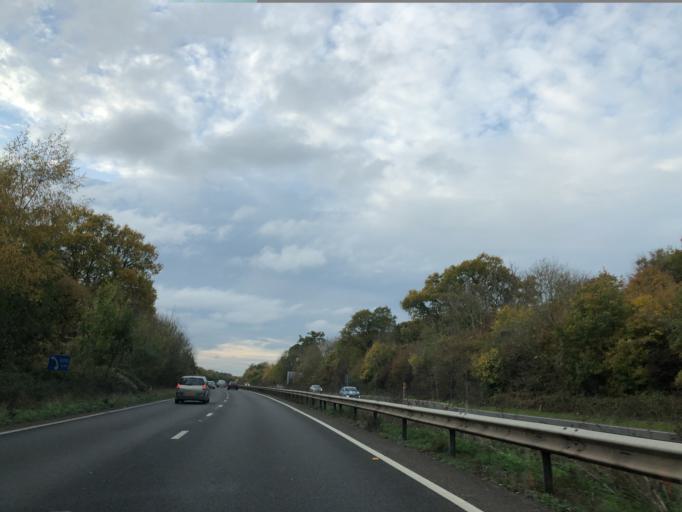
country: GB
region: England
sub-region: Royal Borough of Windsor and Maidenhead
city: Bisham
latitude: 51.5238
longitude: -0.7715
